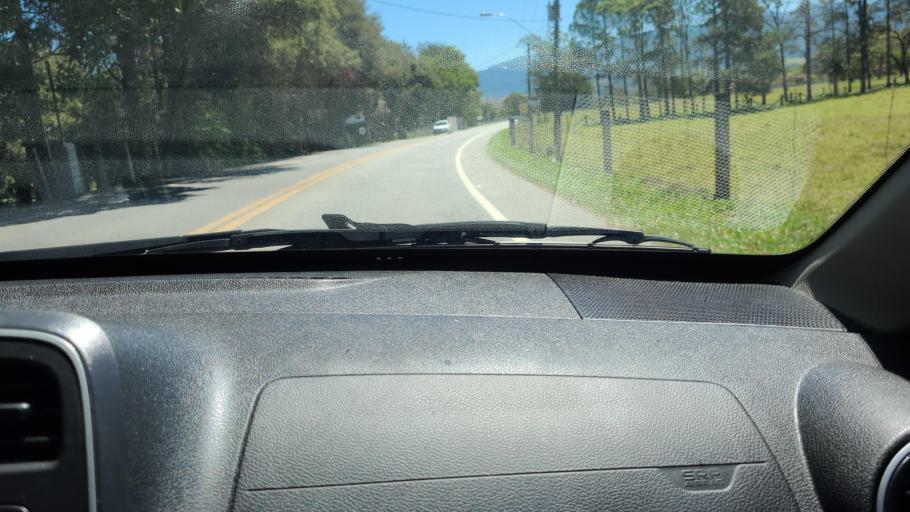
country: BR
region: Sao Paulo
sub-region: Pindamonhangaba
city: Pindamonhangaba
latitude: -22.8981
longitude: -45.4994
